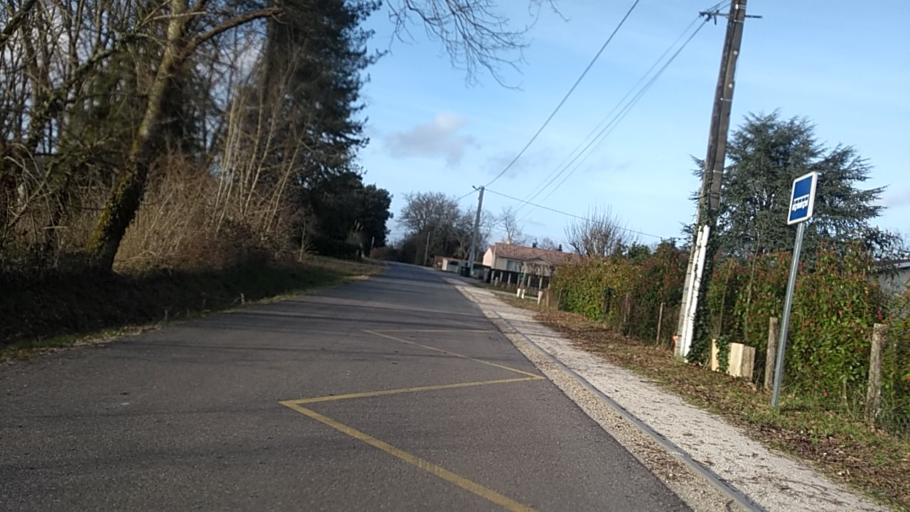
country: FR
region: Aquitaine
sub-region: Departement de la Gironde
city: Le Barp
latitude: 44.5956
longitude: -0.7682
